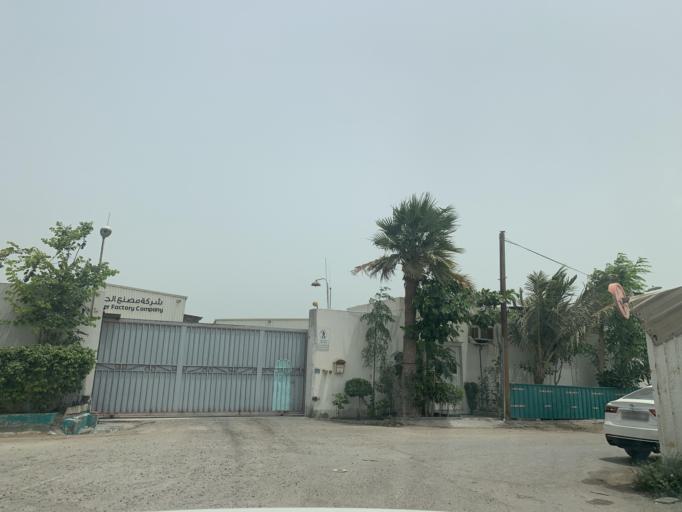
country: BH
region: Manama
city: Jidd Hafs
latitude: 26.2305
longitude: 50.5162
